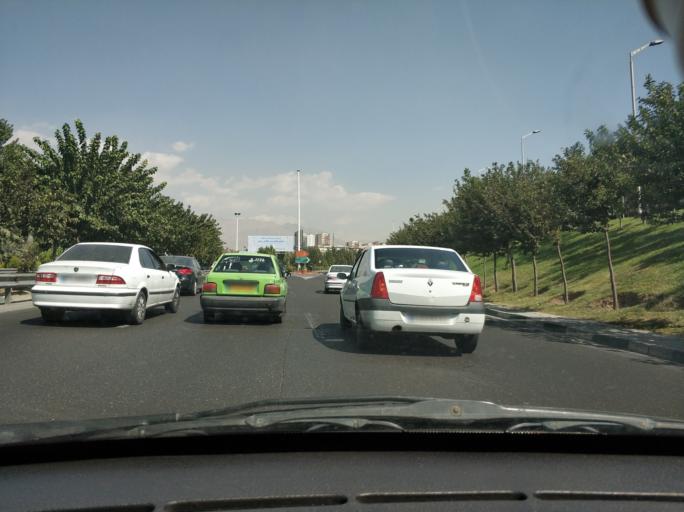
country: IR
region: Tehran
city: Tehran
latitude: 35.7467
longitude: 51.3709
